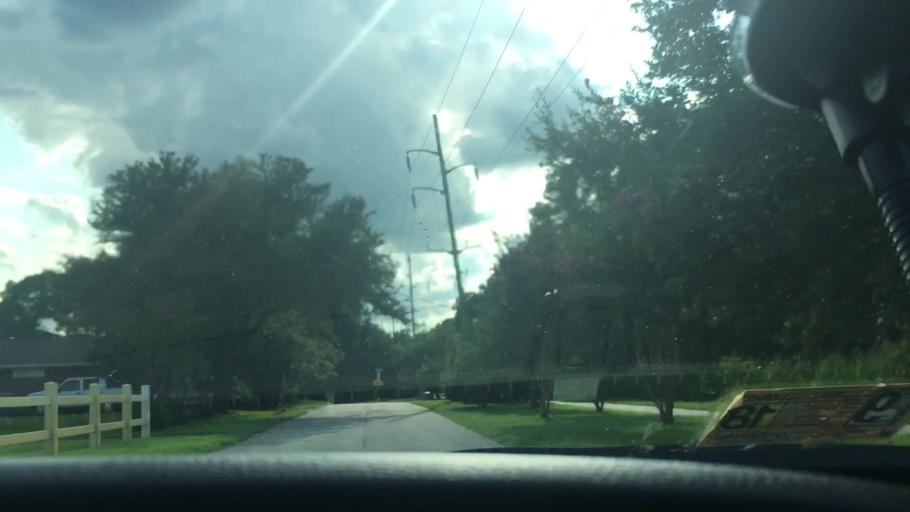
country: US
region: Virginia
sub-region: City of Virginia Beach
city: Virginia Beach
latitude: 36.9089
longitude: -76.0777
